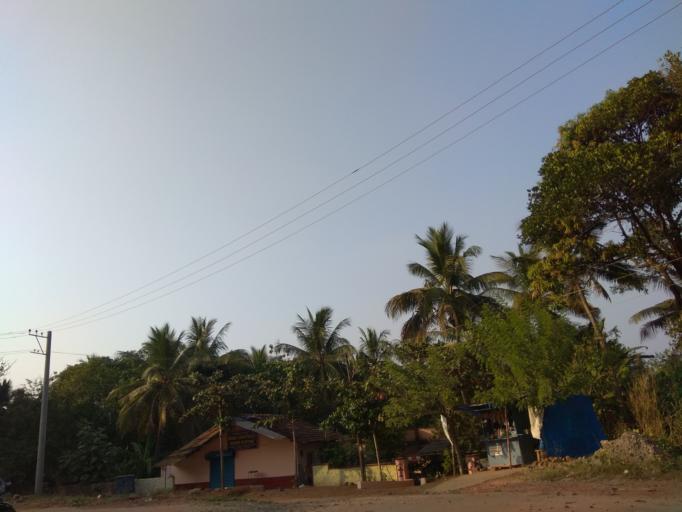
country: IN
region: Karnataka
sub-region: Dakshina Kannada
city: Mangalore
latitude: 12.9106
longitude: 74.8526
